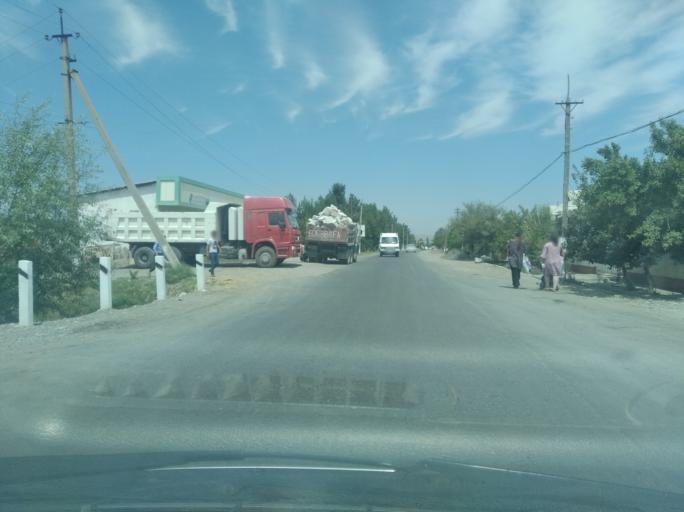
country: KG
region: Osh
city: Aravan
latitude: 40.6104
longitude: 72.4572
